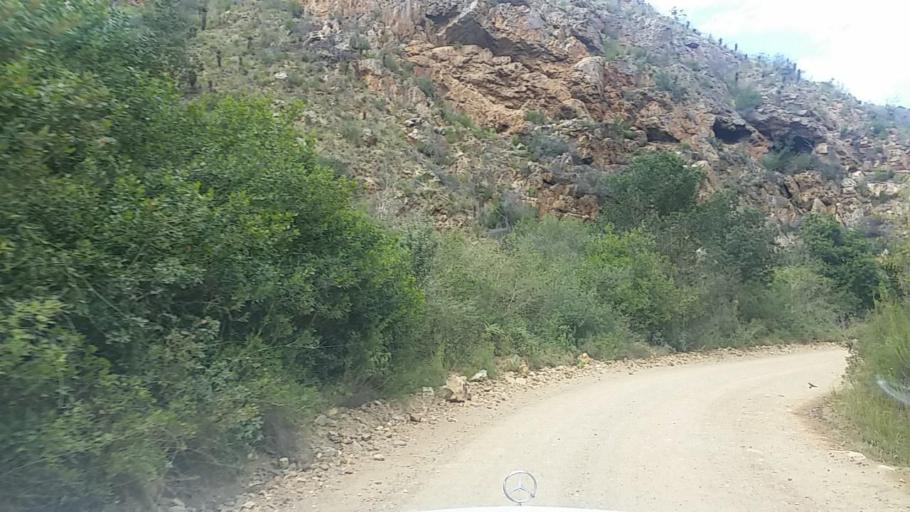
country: ZA
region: Western Cape
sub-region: Eden District Municipality
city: Knysna
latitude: -33.8069
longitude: 23.1810
